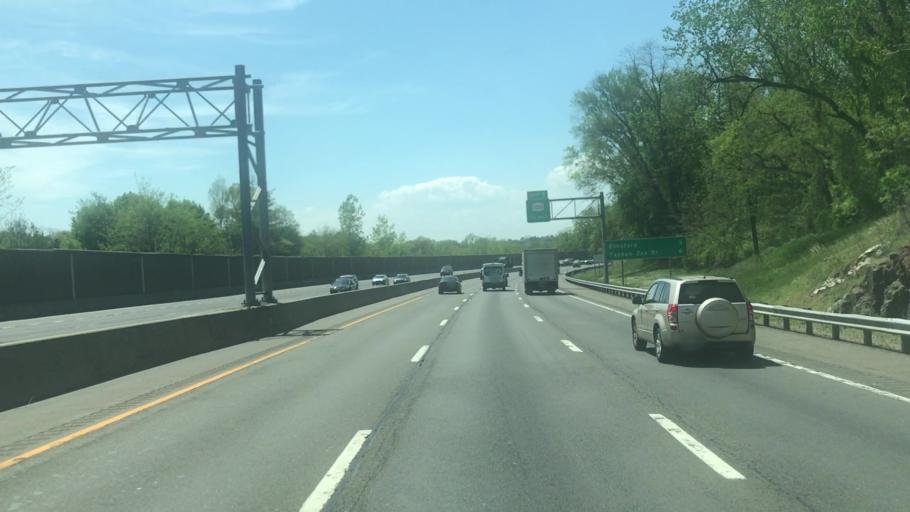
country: US
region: New York
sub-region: Westchester County
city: Fairview
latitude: 41.0428
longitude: -73.7810
